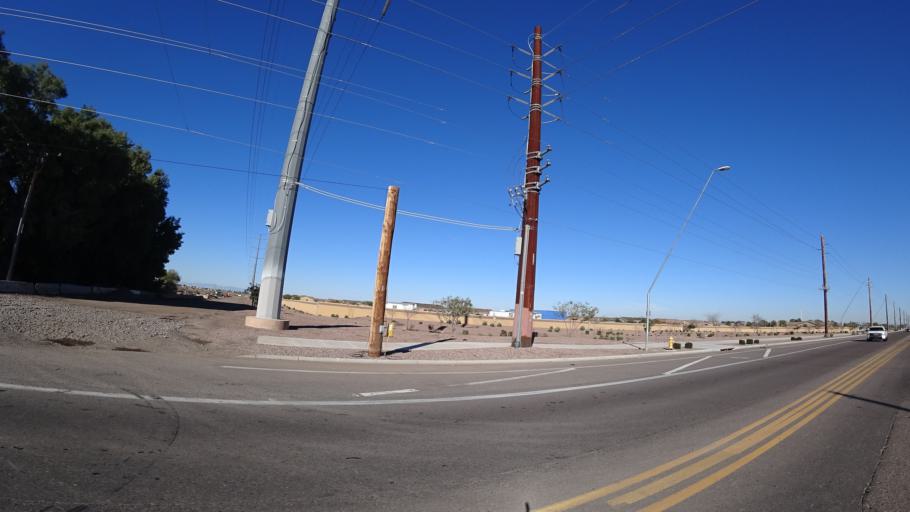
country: US
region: Arizona
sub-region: Maricopa County
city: Laveen
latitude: 33.3919
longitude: -112.1856
